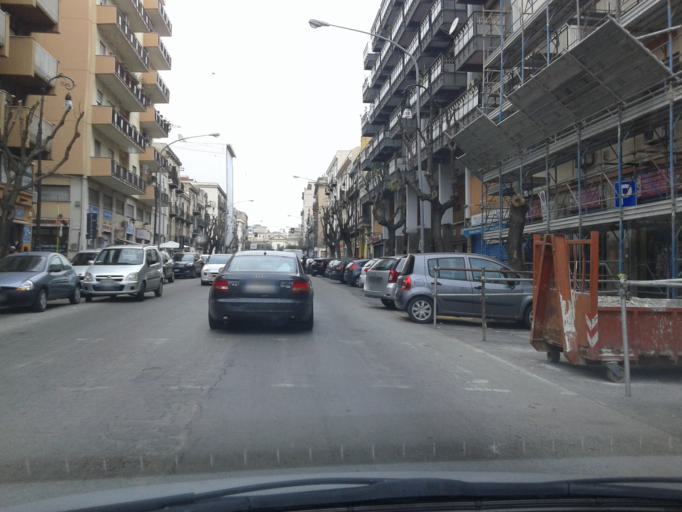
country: IT
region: Sicily
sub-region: Palermo
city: Palermo
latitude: 38.1121
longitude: 13.3696
